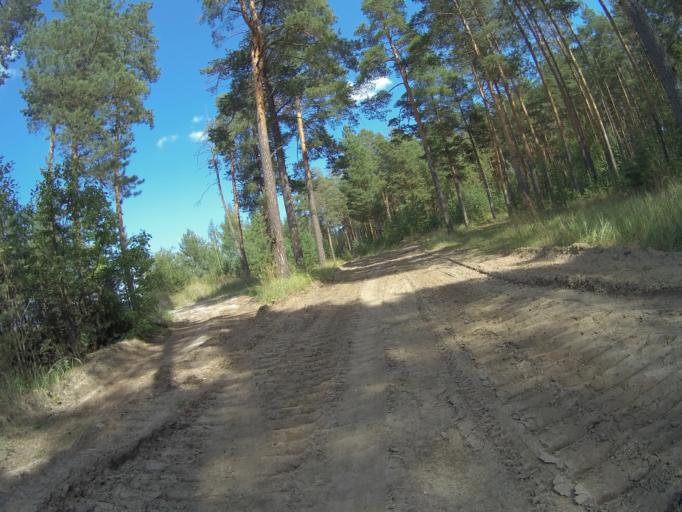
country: RU
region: Vladimir
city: Kommunar
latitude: 56.0386
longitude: 40.4254
